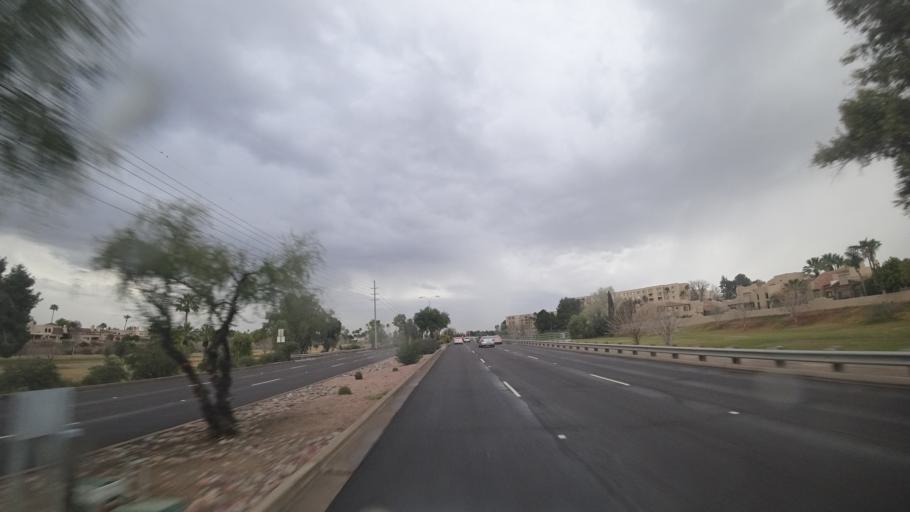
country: US
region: Arizona
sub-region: Maricopa County
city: Scottsdale
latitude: 33.5070
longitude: -111.9088
